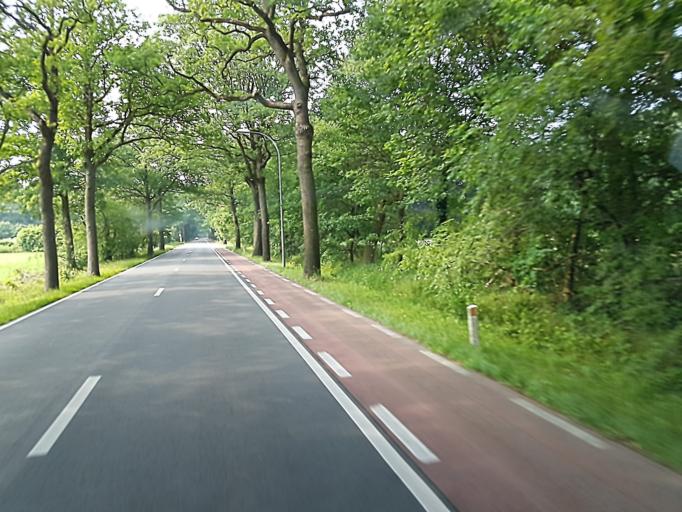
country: BE
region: Flanders
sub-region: Provincie Antwerpen
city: Turnhout
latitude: 51.3584
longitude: 4.9354
